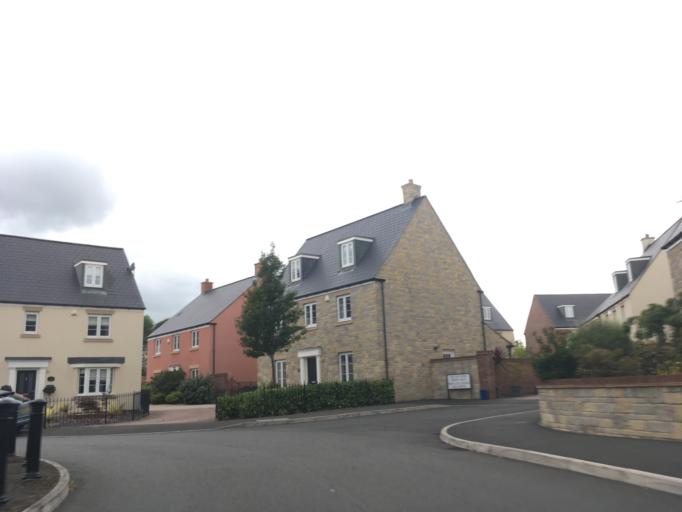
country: GB
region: Wales
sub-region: Monmouthshire
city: Rogiet
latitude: 51.6149
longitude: -2.7695
